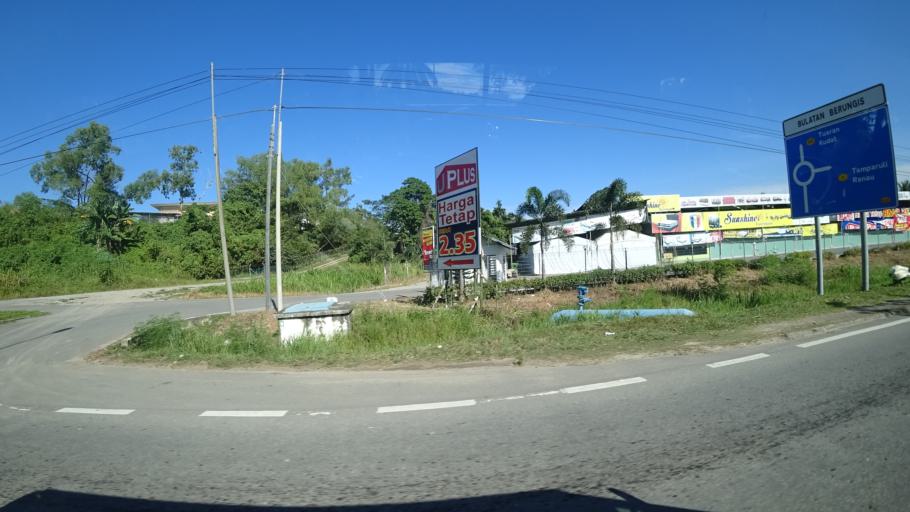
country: MY
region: Sabah
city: Kota Kinabalu
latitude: 6.1448
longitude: 116.2210
